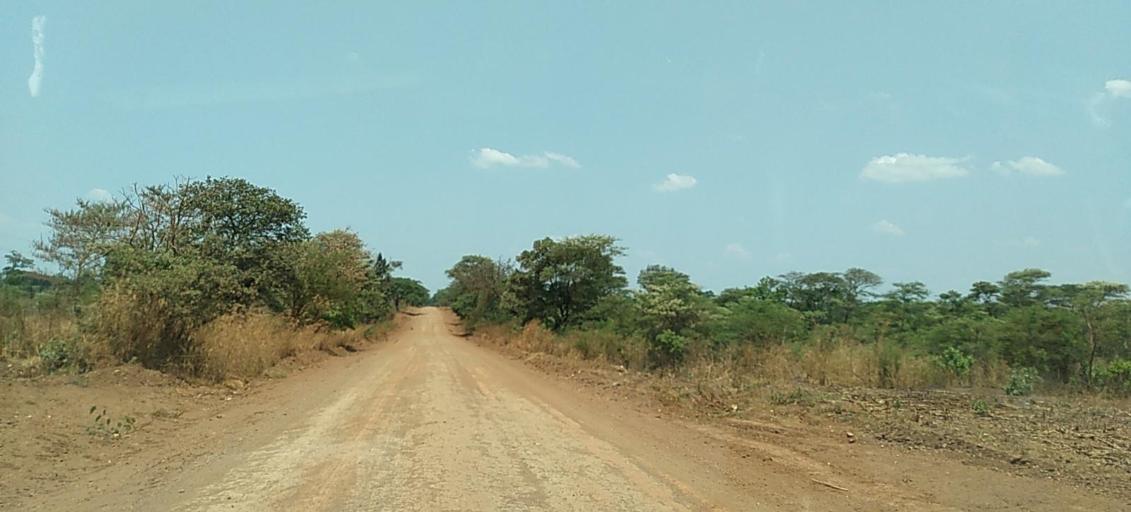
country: ZM
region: Copperbelt
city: Mpongwe
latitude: -13.5170
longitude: 27.9885
